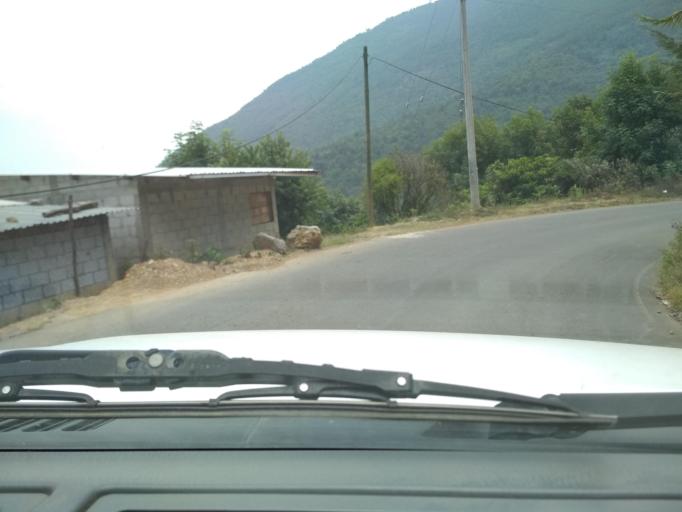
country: MX
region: Veracruz
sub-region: Camerino Z. Mendoza
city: La Cuesta
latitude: 18.7899
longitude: -97.1660
